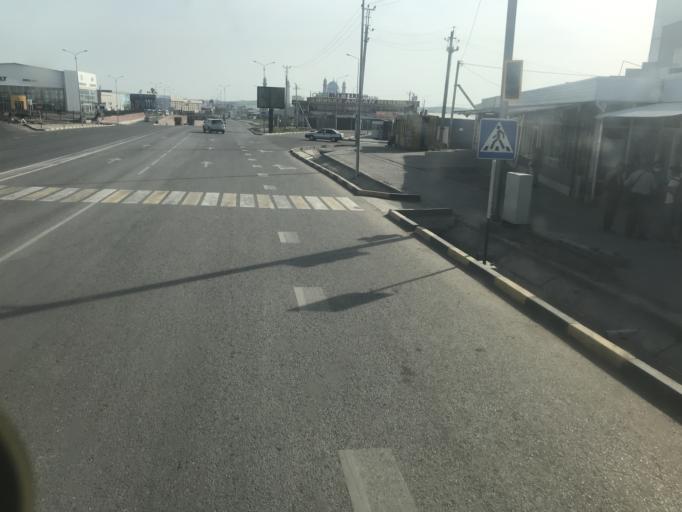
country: KZ
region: Ongtustik Qazaqstan
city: Shymkent
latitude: 42.3549
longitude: 69.5329
